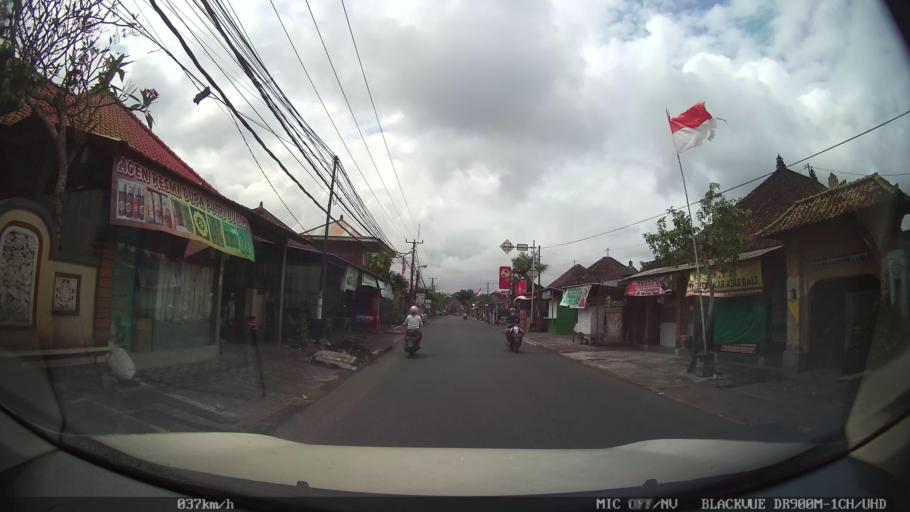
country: ID
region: Bali
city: Banjar Bucu
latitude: -8.5835
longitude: 115.1923
